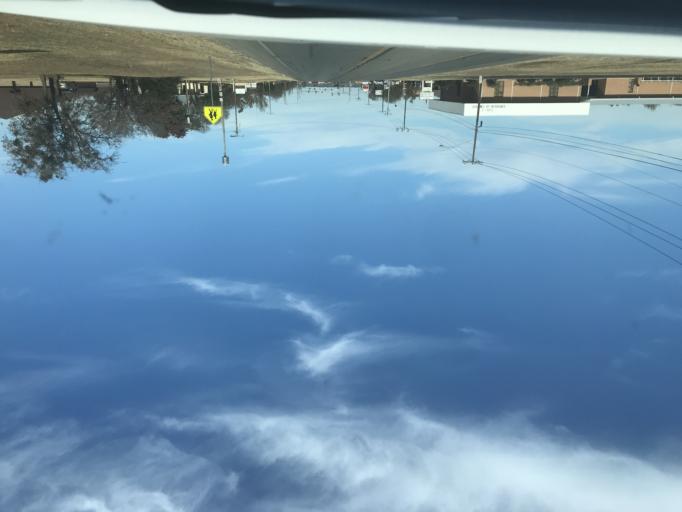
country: US
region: Texas
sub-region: Erath County
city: Stephenville
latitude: 32.2180
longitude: -98.2392
